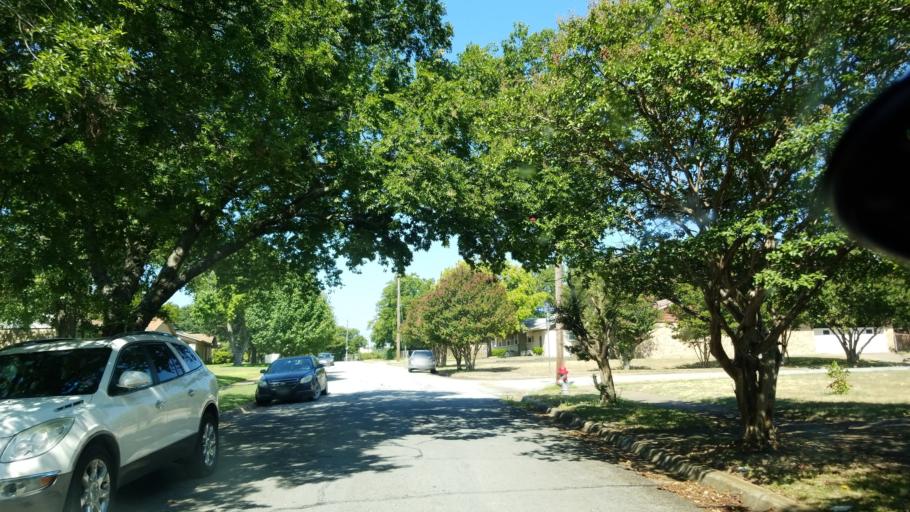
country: US
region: Texas
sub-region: Dallas County
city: Duncanville
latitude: 32.6570
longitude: -96.9041
